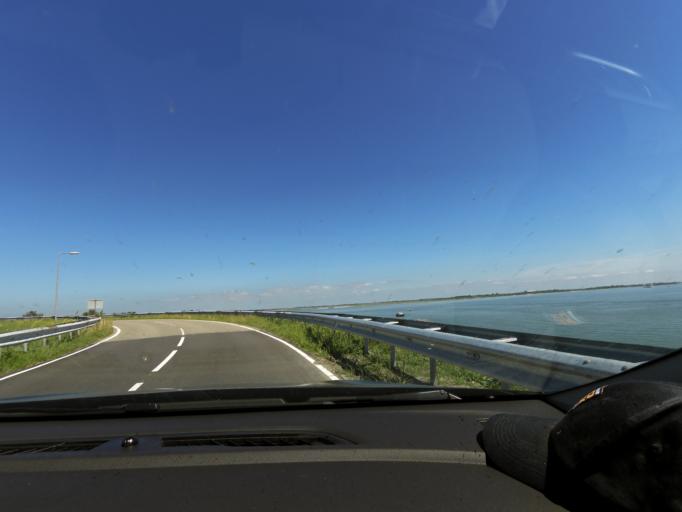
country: NL
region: Friesland
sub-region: Sudwest Fryslan
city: Makkum
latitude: 53.0739
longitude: 5.3418
